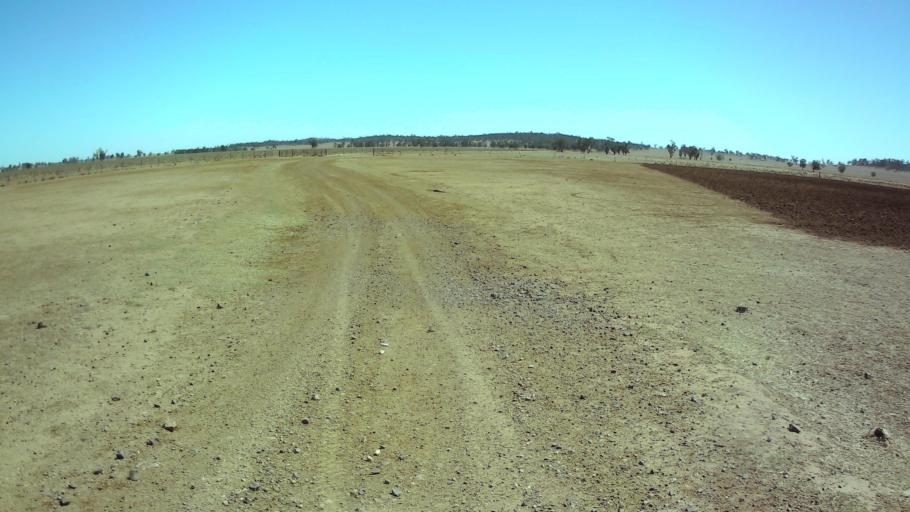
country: AU
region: New South Wales
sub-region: Forbes
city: Forbes
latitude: -33.7046
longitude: 147.6688
